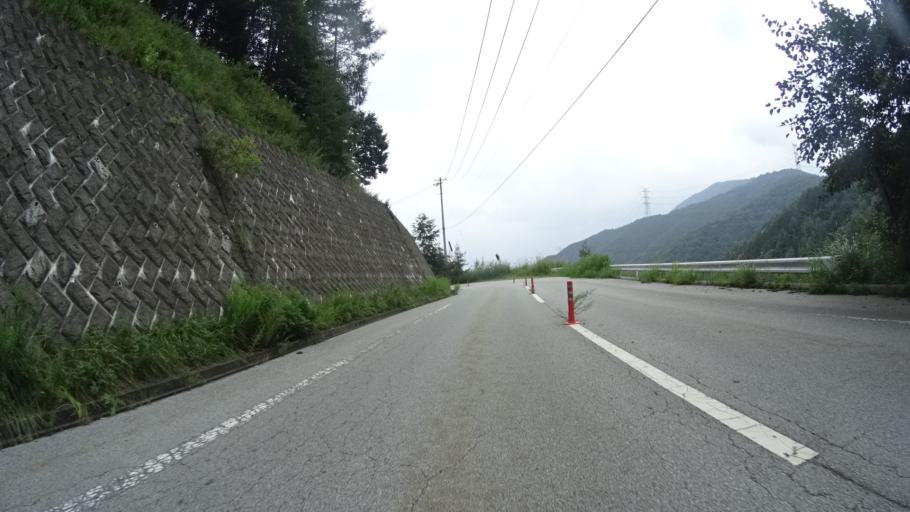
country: JP
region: Yamanashi
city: Enzan
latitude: 35.8057
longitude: 138.6645
